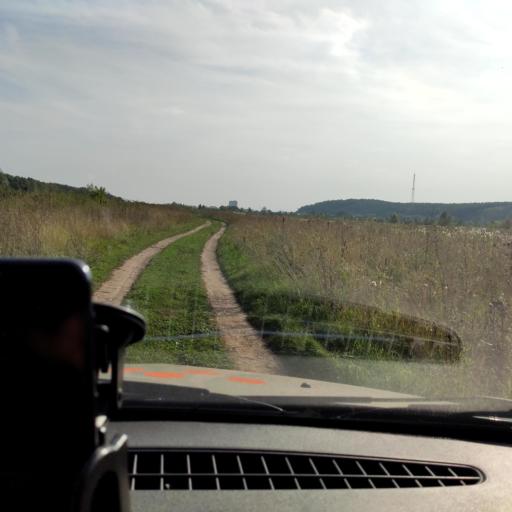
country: RU
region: Bashkortostan
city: Ufa
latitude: 54.8238
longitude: 56.1616
